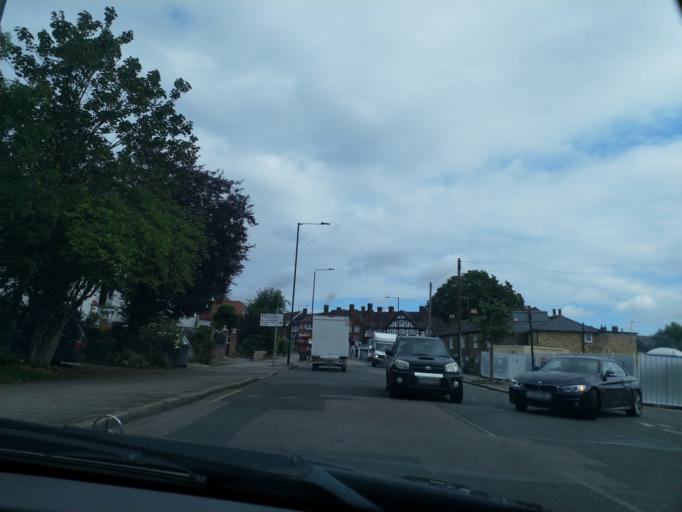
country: GB
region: England
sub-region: Greater London
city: Harrow on the Hill
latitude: 51.5608
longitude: -0.3196
